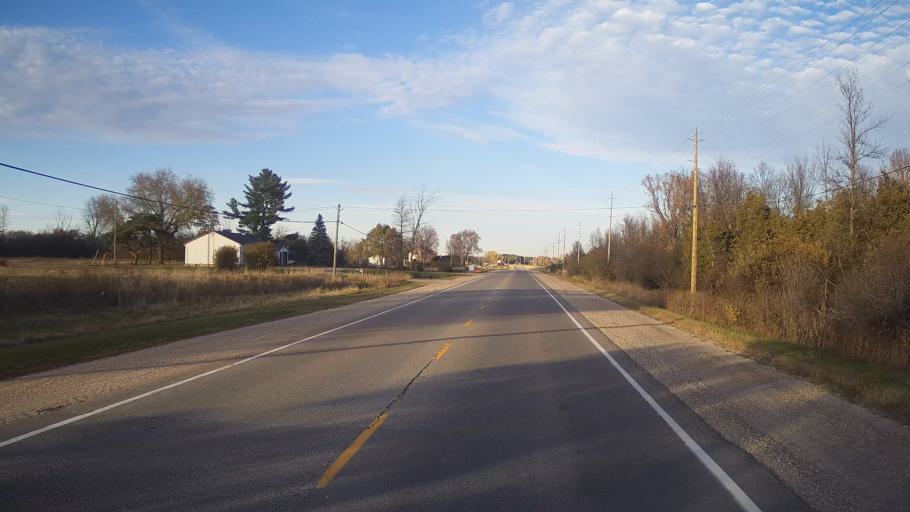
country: CA
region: Ontario
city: Perth
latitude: 44.9252
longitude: -76.2494
